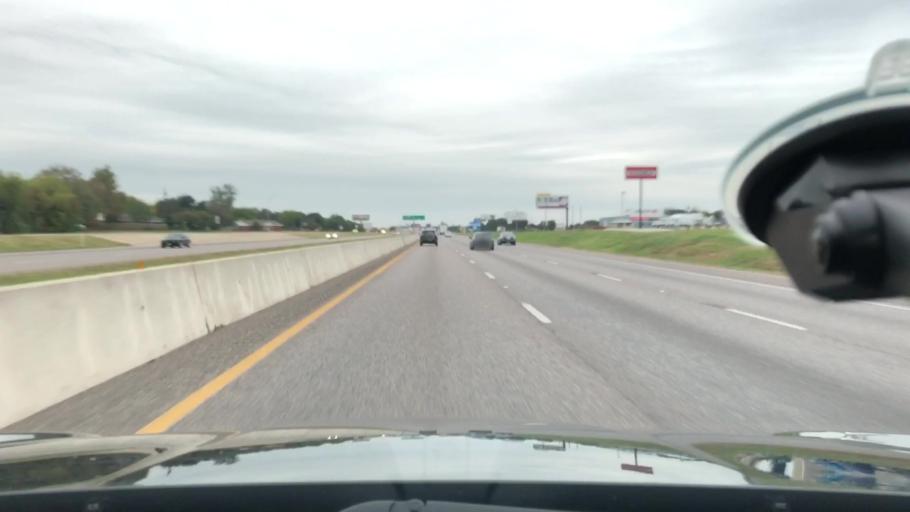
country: US
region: Texas
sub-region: McLennan County
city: Lacy-Lakeview
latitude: 31.6181
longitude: -97.0998
